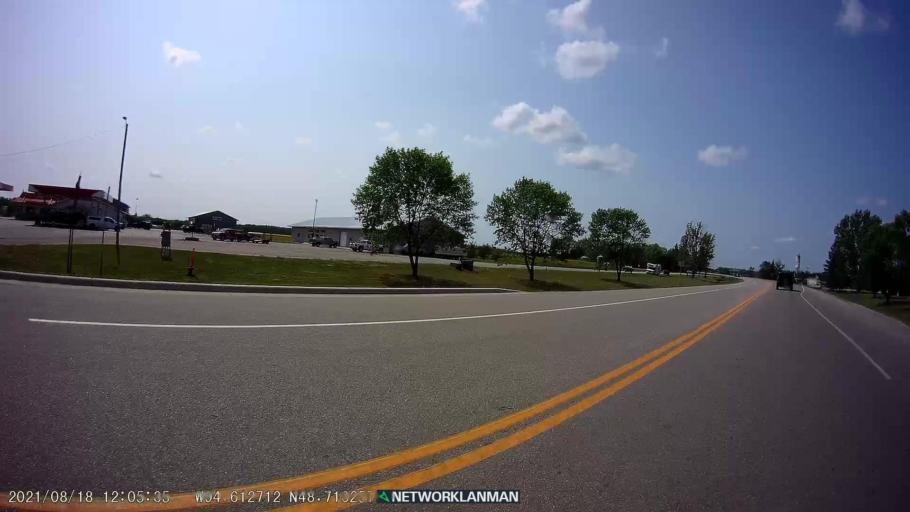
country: US
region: Minnesota
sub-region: Lake of the Woods County
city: Baudette
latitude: 48.7133
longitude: -94.6127
